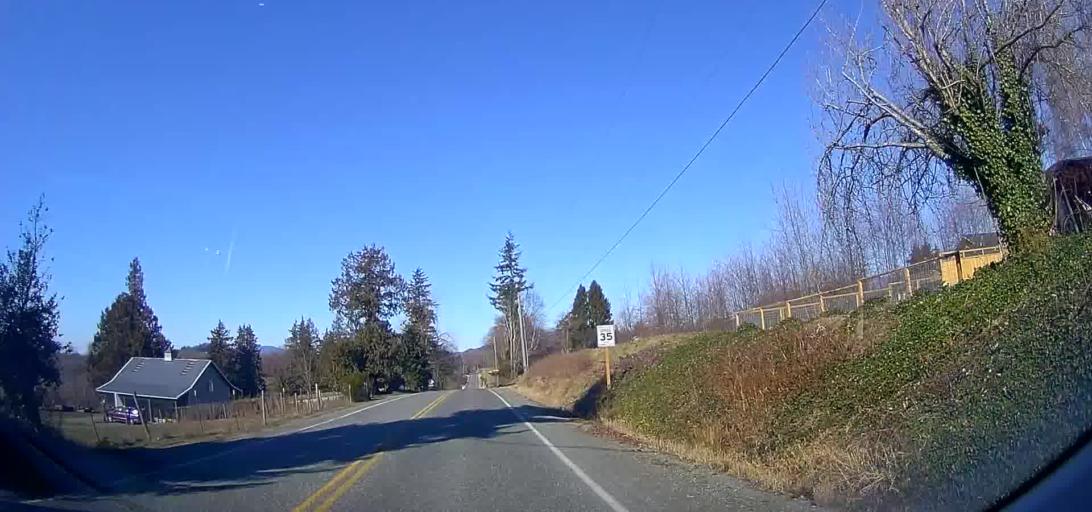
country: US
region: Washington
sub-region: Skagit County
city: Burlington
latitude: 48.4544
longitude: -122.3028
